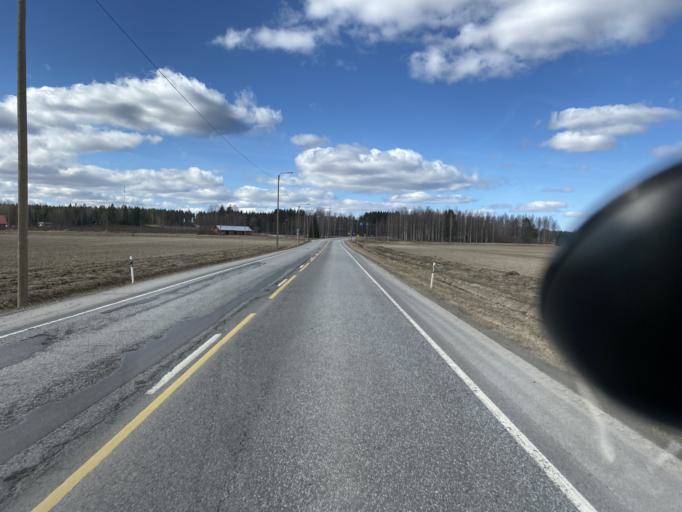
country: FI
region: Satakunta
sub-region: Pori
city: Huittinen
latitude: 61.1775
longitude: 22.5871
